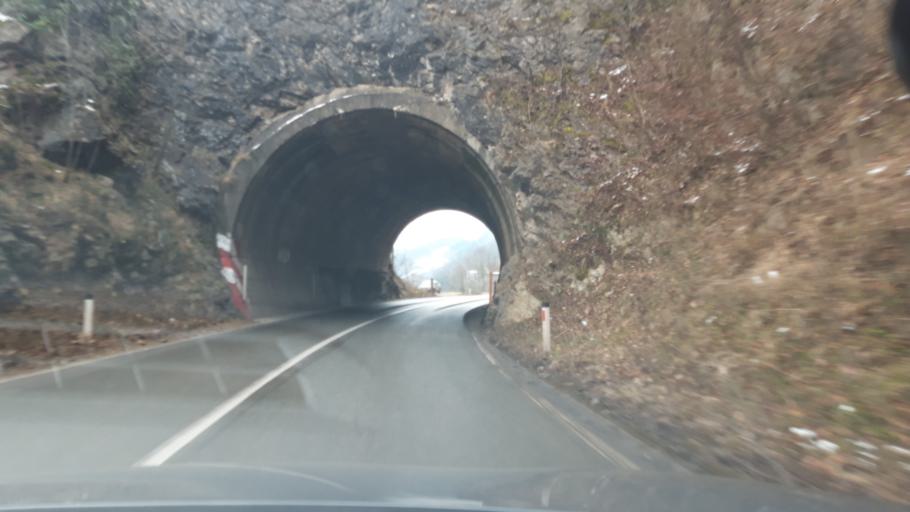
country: RS
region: Central Serbia
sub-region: Macvanski Okrug
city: Mali Zvornik
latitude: 44.3175
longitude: 19.1279
